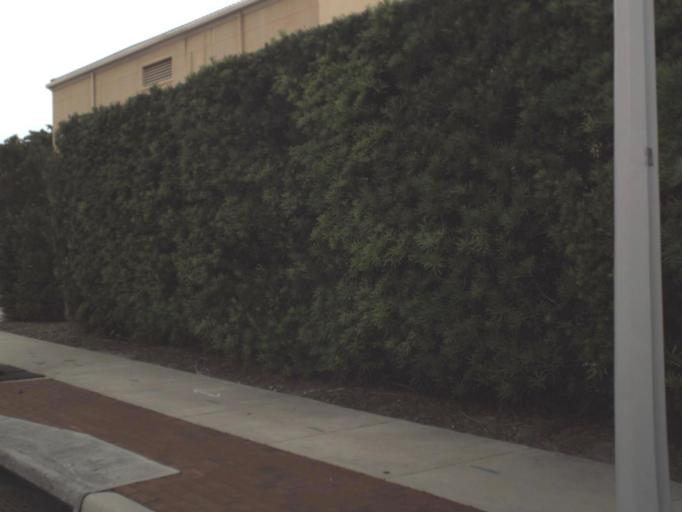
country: US
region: Florida
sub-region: Lee County
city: North Fort Myers
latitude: 26.6444
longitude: -81.8714
